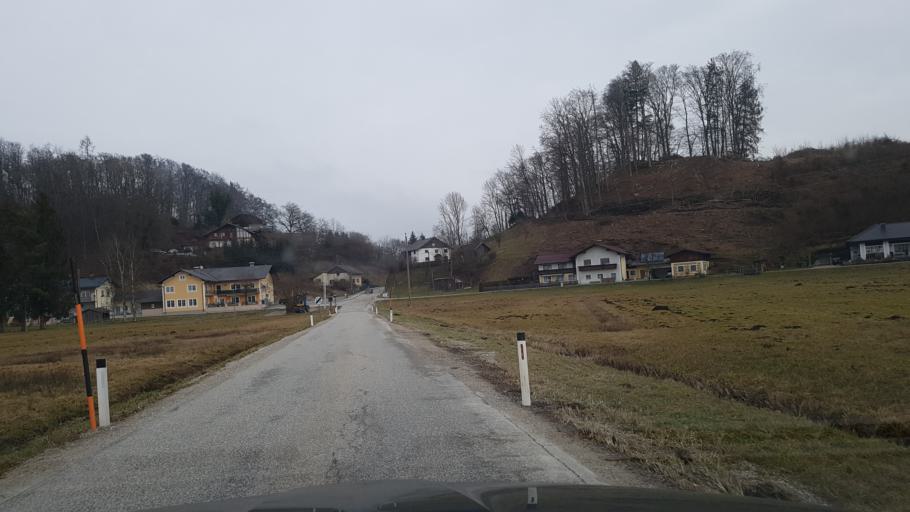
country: AT
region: Salzburg
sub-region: Politischer Bezirk Salzburg-Umgebung
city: Dorfbeuern
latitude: 48.0630
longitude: 12.9614
